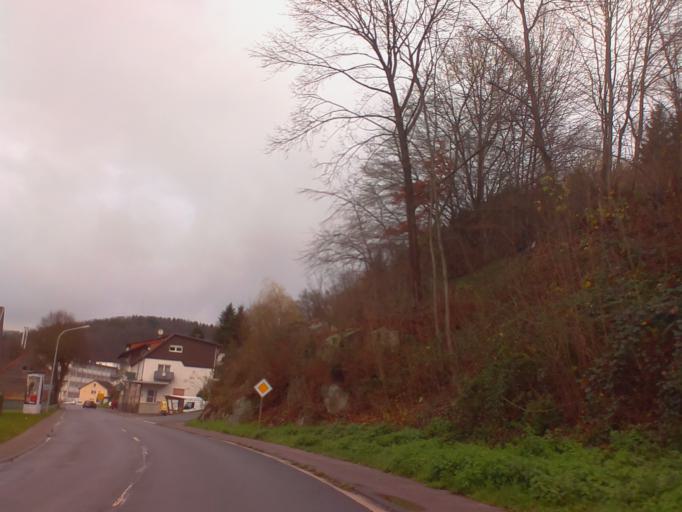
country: DE
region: Hesse
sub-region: Regierungsbezirk Darmstadt
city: Wald-Michelbach
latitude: 49.5657
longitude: 8.8447
